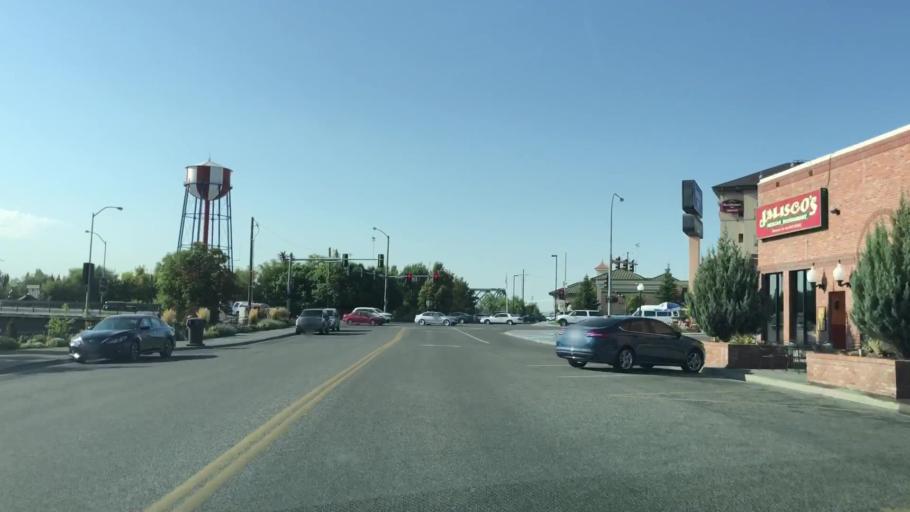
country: US
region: Idaho
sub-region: Bonneville County
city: Idaho Falls
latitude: 43.4942
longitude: -112.0451
